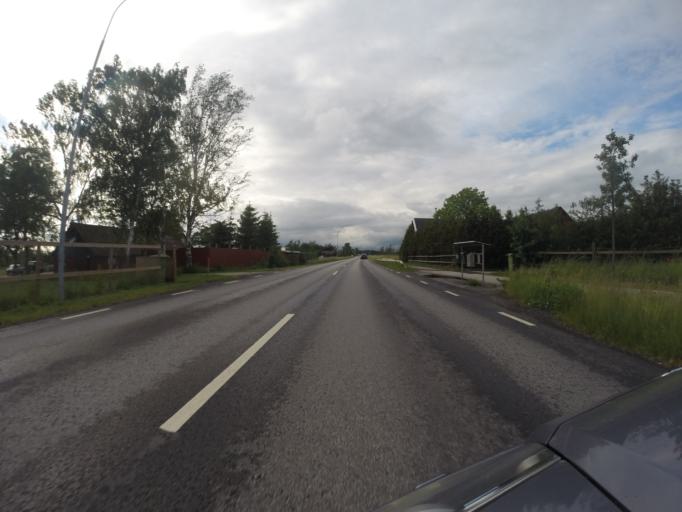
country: SE
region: Skane
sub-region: Kavlinge Kommun
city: Loddekopinge
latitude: 55.7895
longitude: 13.0004
